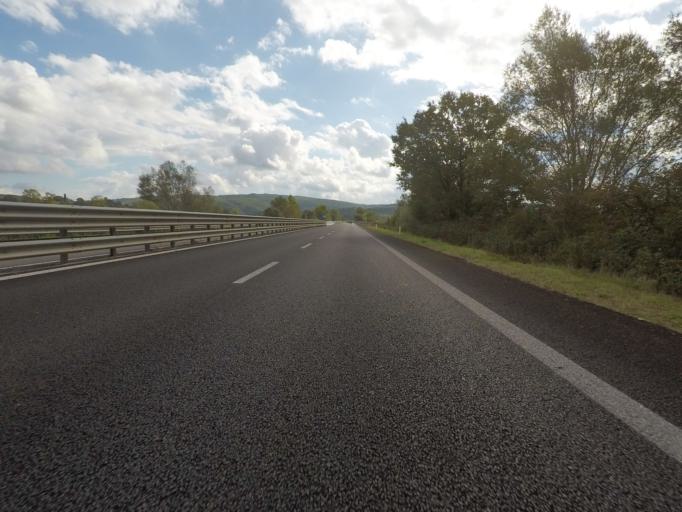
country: IT
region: Tuscany
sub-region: Provincia di Siena
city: Serre di Rapolano
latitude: 43.2517
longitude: 11.6394
